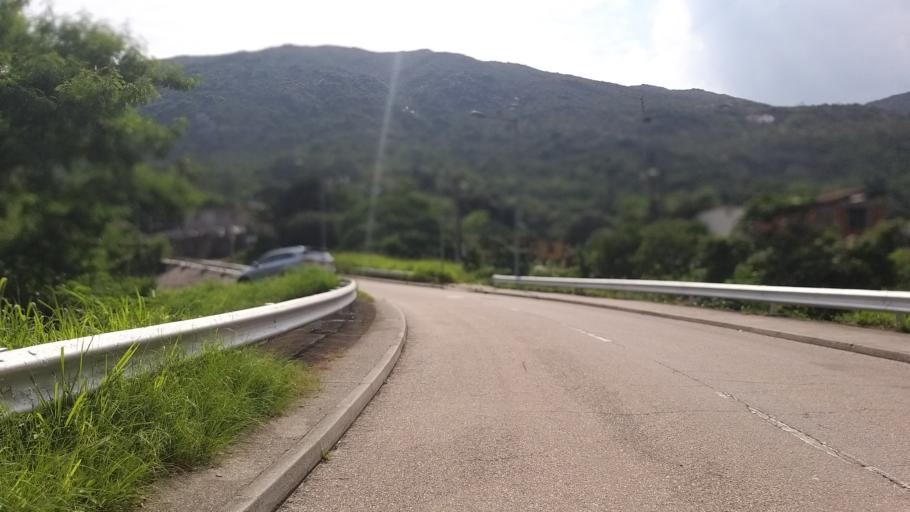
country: HK
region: Tuen Mun
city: Tuen Mun
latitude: 22.4194
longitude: 113.9713
